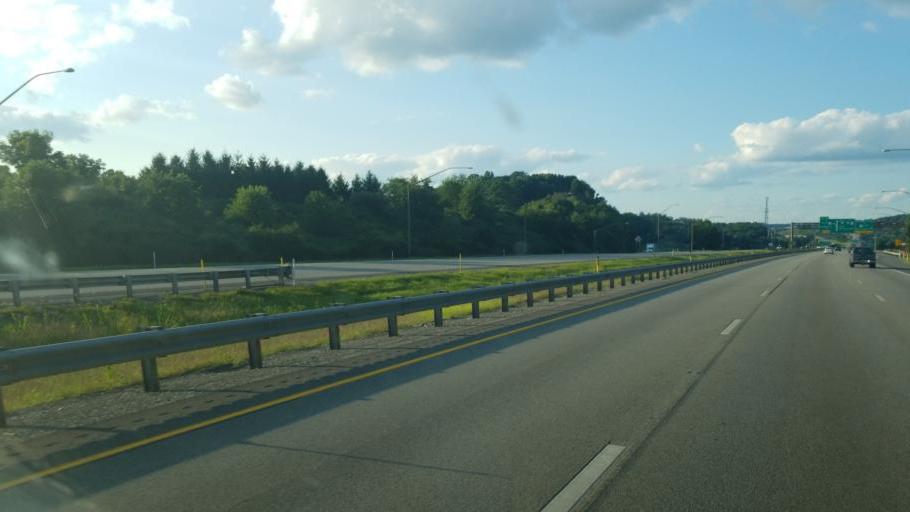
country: US
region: Pennsylvania
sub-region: Allegheny County
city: Bradford Woods
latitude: 40.6427
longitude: -80.0970
